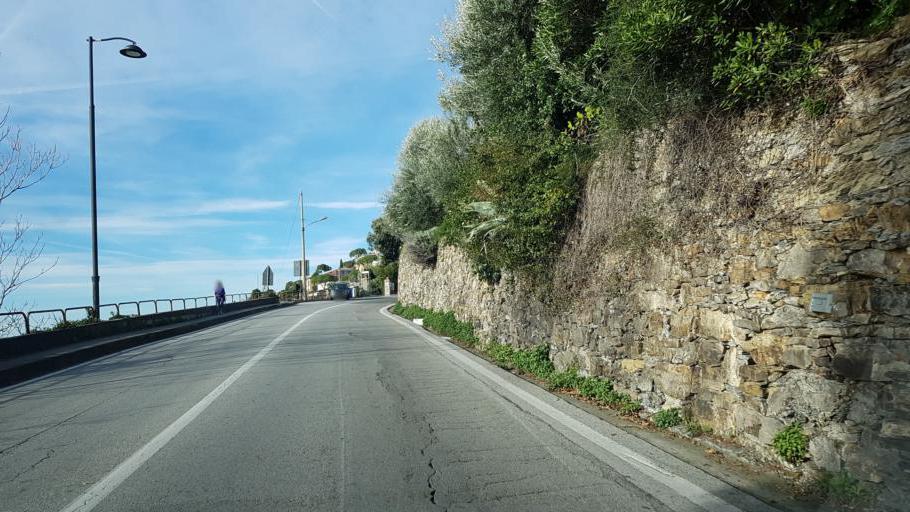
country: IT
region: Liguria
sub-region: Provincia di Genova
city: Recco
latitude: 44.3641
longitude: 9.1250
